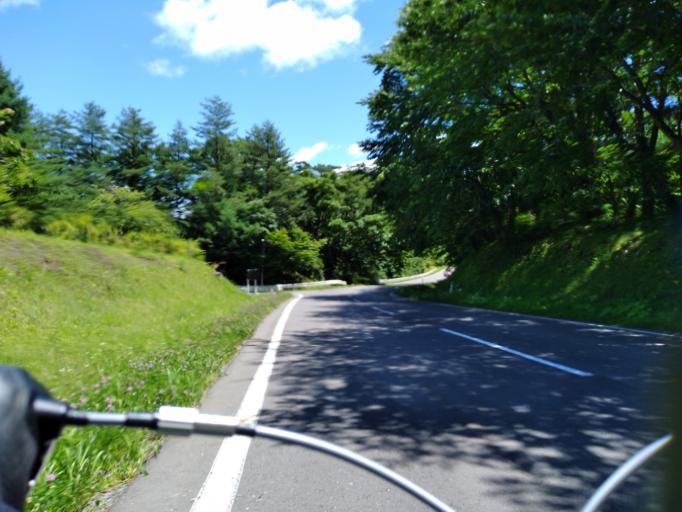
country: JP
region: Iwate
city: Shizukuishi
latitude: 39.7564
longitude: 141.0151
